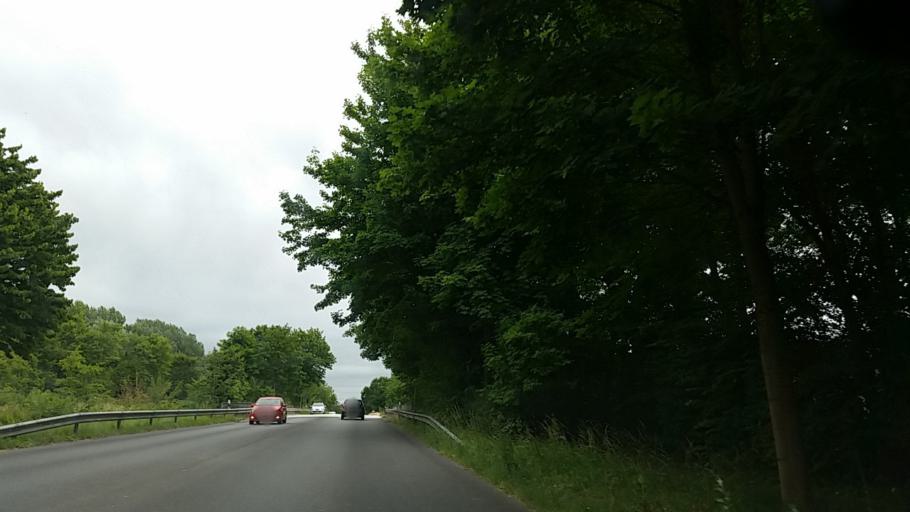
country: DE
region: Schleswig-Holstein
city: Windeby
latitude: 54.4837
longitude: 9.8123
